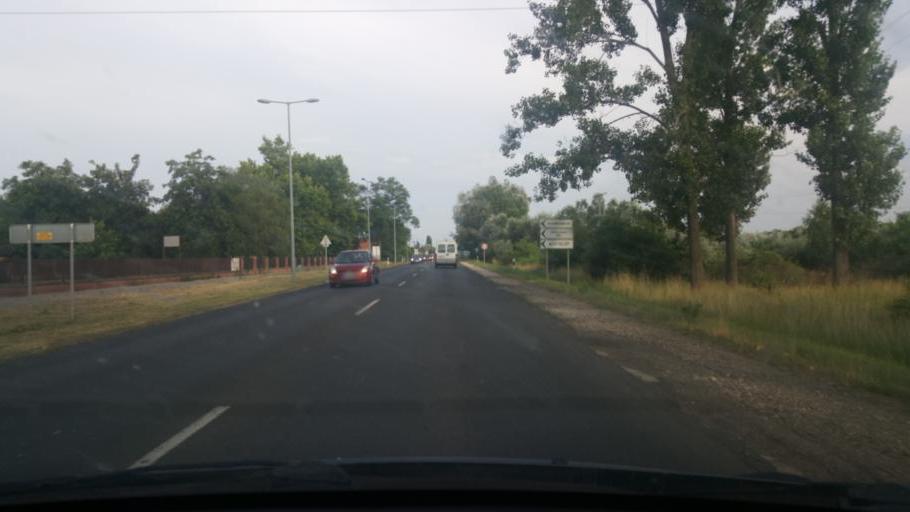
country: HU
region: Pest
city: Monor
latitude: 47.3470
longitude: 19.4159
